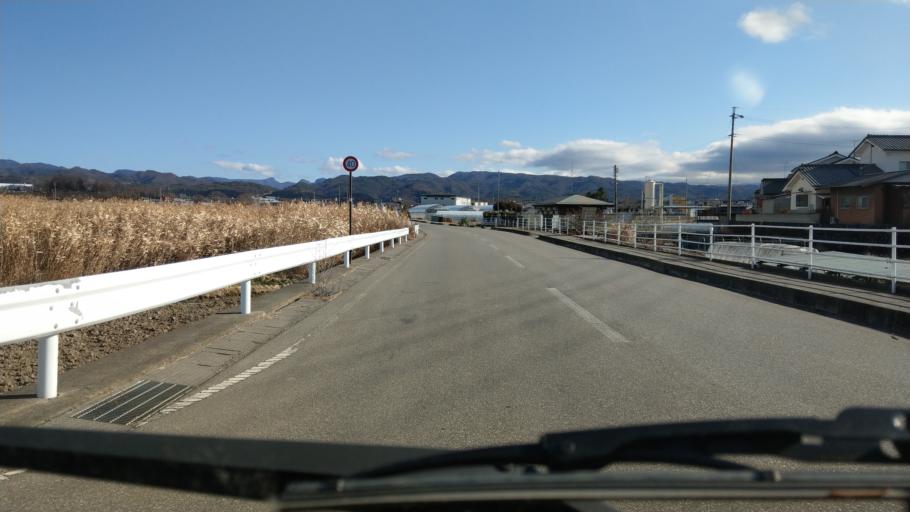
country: JP
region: Nagano
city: Saku
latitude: 36.2447
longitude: 138.4640
